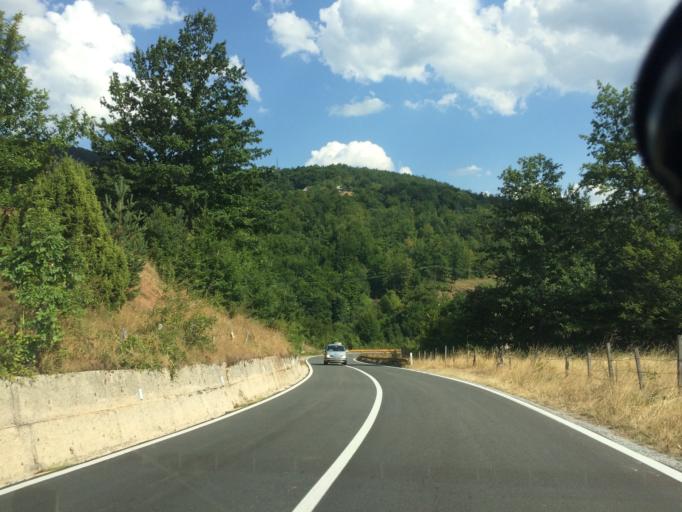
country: ME
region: Opstina Zabljak
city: Zabljak
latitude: 43.1578
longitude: 19.2945
